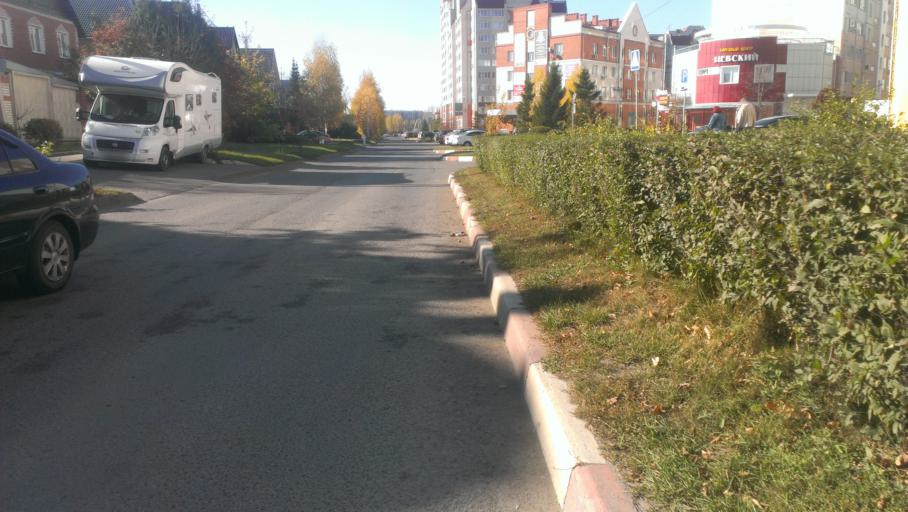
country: RU
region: Altai Krai
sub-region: Gorod Barnaulskiy
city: Barnaul
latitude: 53.3559
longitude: 83.6948
